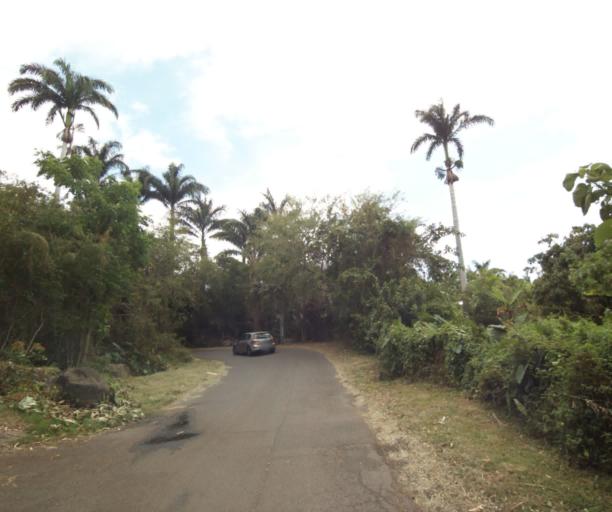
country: RE
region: Reunion
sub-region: Reunion
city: Saint-Paul
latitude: -21.0004
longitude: 55.3013
